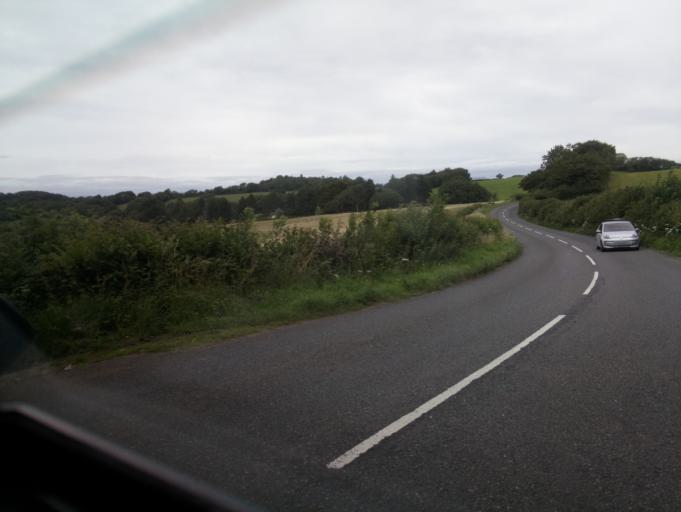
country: GB
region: England
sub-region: North Somerset
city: Churchill
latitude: 51.3211
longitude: -2.7983
